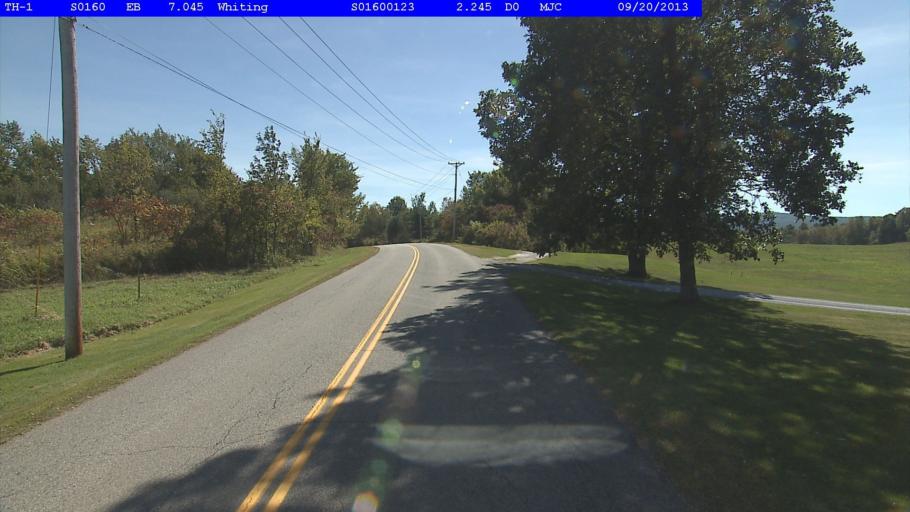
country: US
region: Vermont
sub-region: Rutland County
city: Brandon
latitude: 43.8566
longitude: -73.1844
